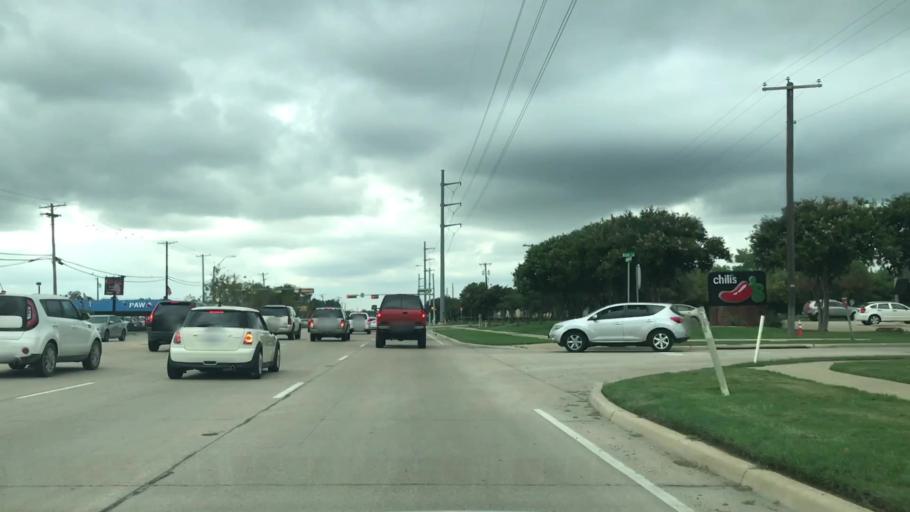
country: US
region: Texas
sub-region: Dallas County
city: Rowlett
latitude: 32.9080
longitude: -96.5794
